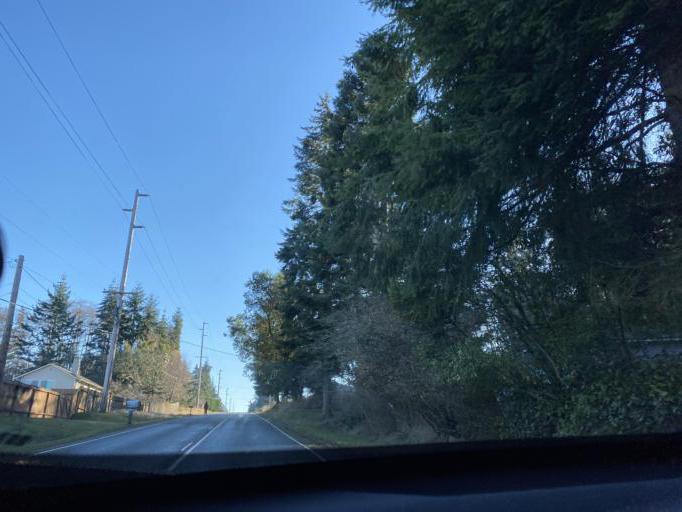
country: US
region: Washington
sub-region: Island County
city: Camano
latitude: 48.1289
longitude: -122.5673
